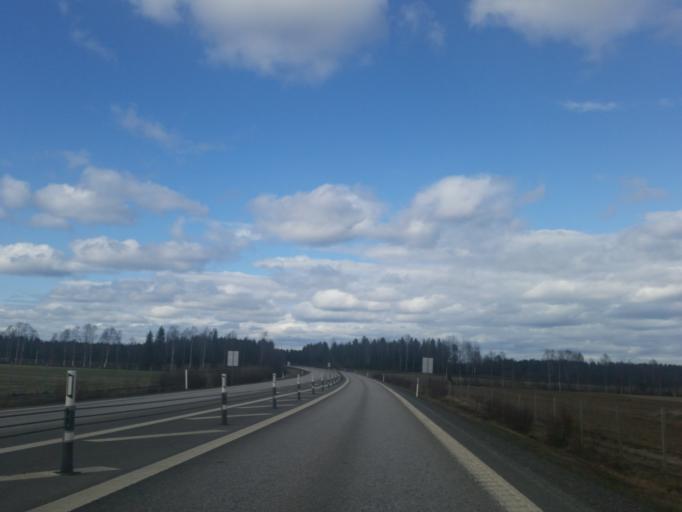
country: SE
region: Vaesterbotten
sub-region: Robertsfors Kommun
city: Robertsfors
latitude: 64.0799
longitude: 20.8659
